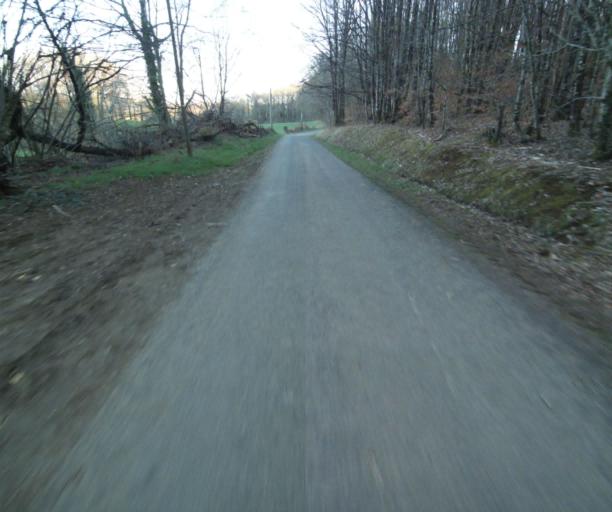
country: FR
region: Limousin
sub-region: Departement de la Correze
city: Seilhac
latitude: 45.3506
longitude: 1.7204
